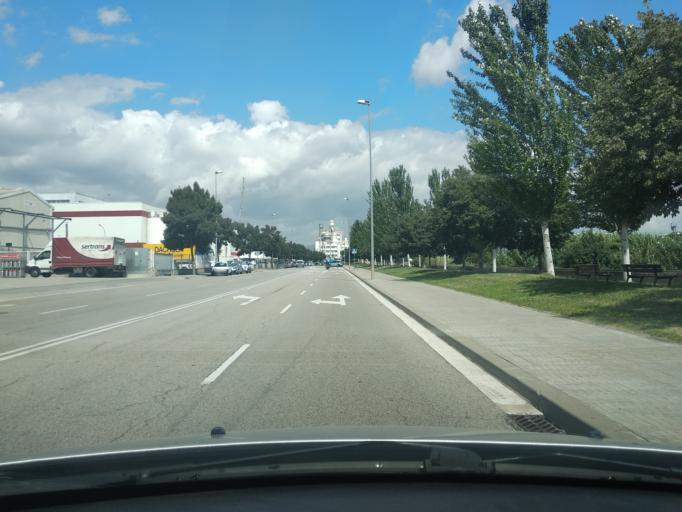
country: ES
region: Catalonia
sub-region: Provincia de Barcelona
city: Granollers
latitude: 41.6050
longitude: 2.2790
